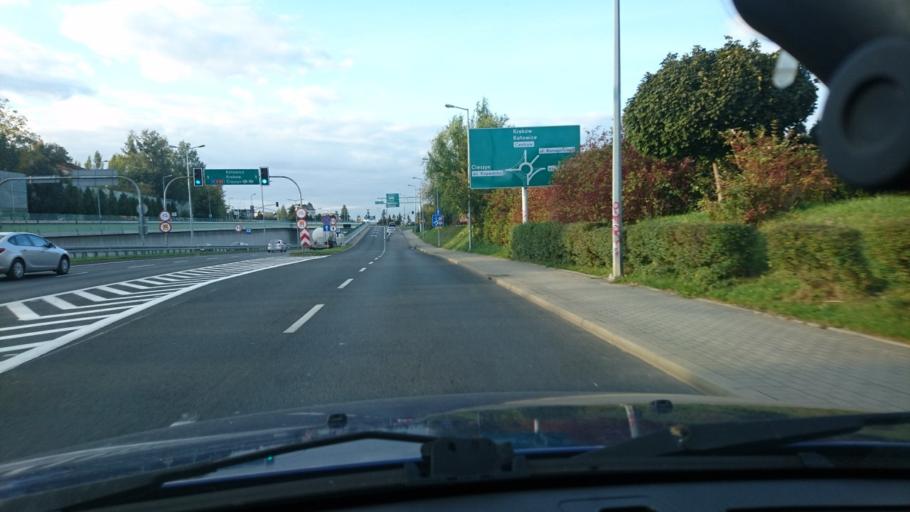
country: PL
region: Silesian Voivodeship
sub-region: Bielsko-Biala
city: Bielsko-Biala
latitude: 49.8137
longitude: 19.0236
